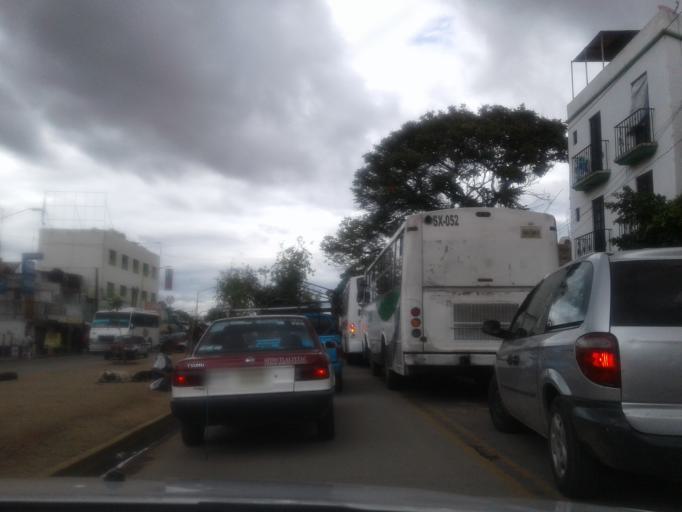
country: MX
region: Oaxaca
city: Oaxaca de Juarez
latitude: 17.0576
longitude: -96.7312
